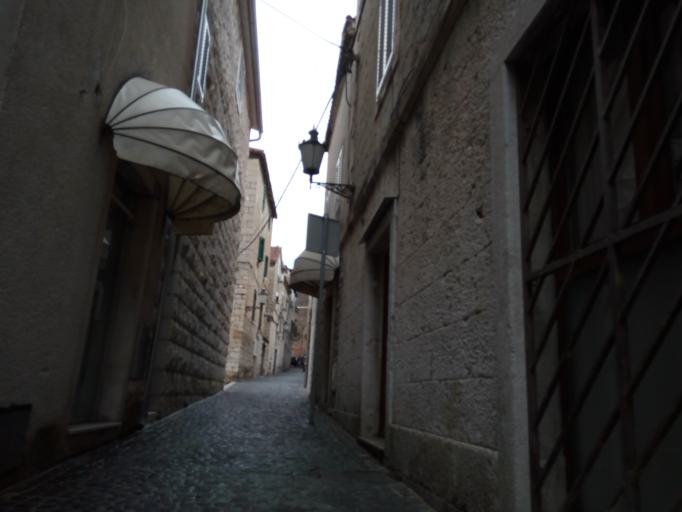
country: HR
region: Splitsko-Dalmatinska
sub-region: Grad Split
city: Split
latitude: 43.5097
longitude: 16.4352
